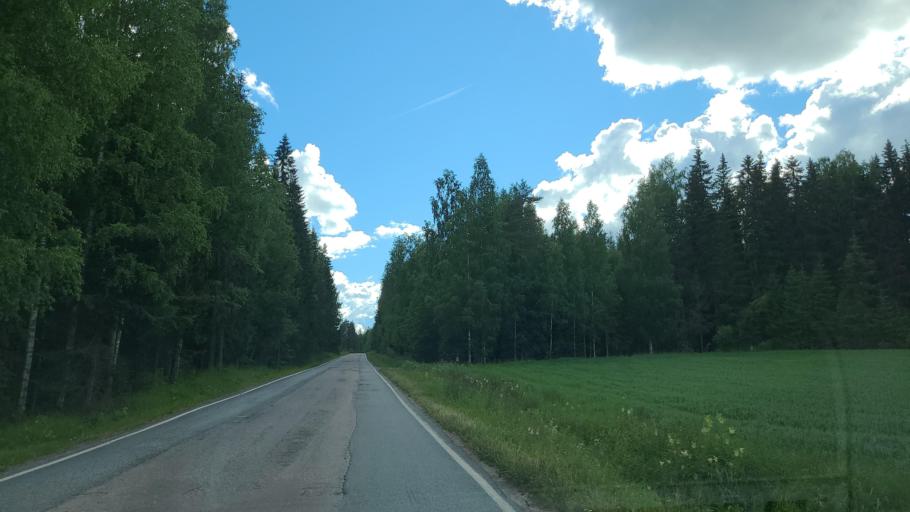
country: FI
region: Central Finland
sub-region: Jaemsae
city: Jaemsae
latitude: 61.8917
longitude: 25.2546
